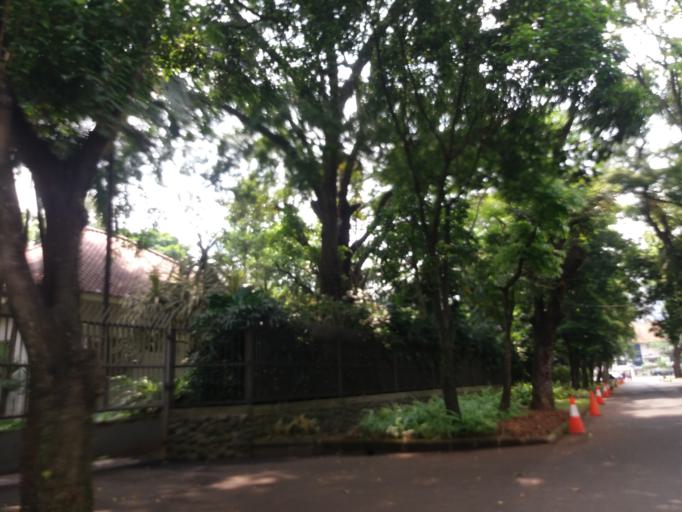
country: ID
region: Jakarta Raya
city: Jakarta
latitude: -6.2305
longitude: 106.8015
